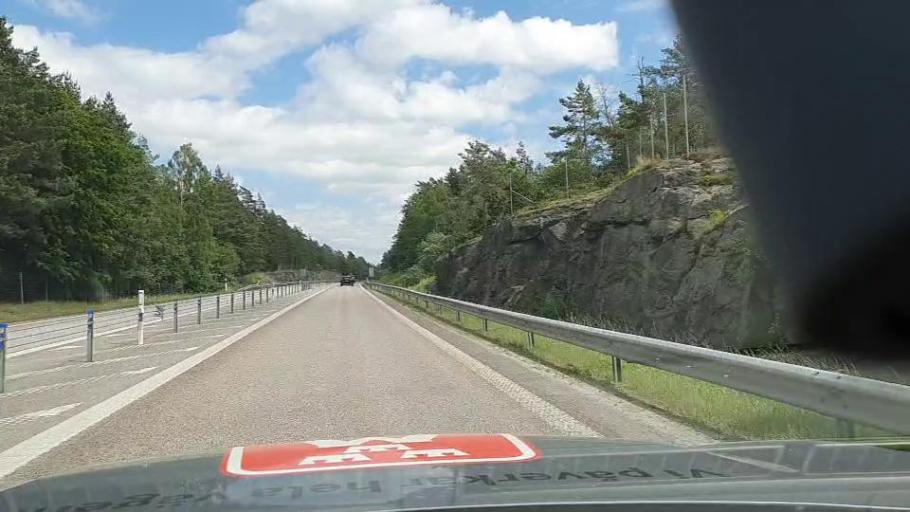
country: SE
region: Blekinge
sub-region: Ronneby Kommun
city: Brakne-Hoby
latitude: 56.2212
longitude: 15.1409
